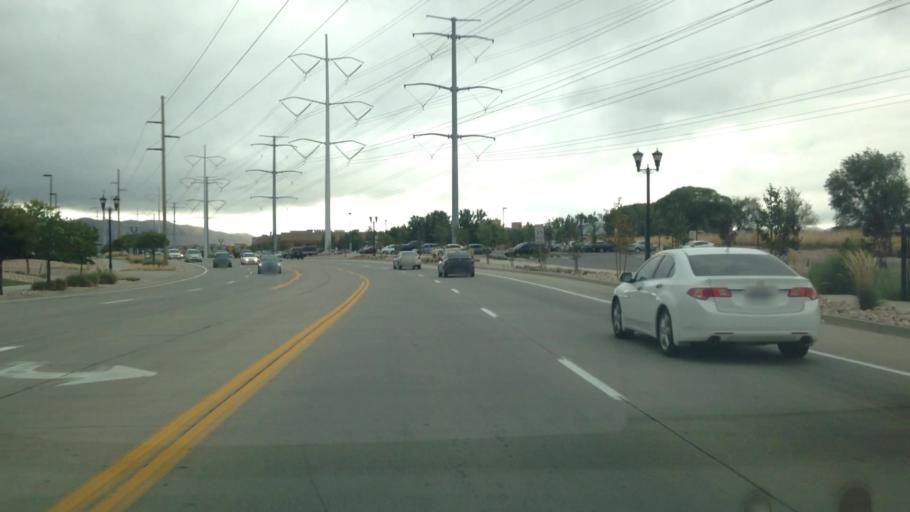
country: US
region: Utah
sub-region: Salt Lake County
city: South Jordan
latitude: 40.5692
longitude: -111.9045
